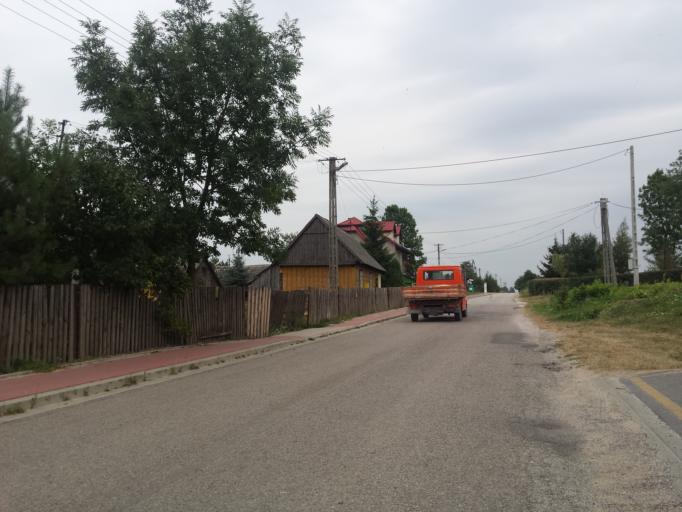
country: PL
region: Swietokrzyskie
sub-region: Powiat kielecki
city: Morawica
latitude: 50.7314
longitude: 20.6821
